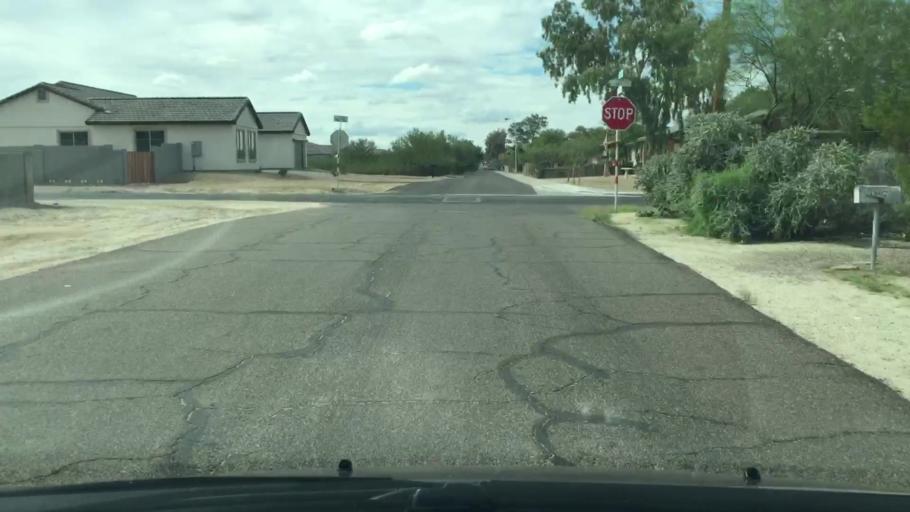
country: US
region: Arizona
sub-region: Maricopa County
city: Phoenix
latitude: 33.3669
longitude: -112.0484
